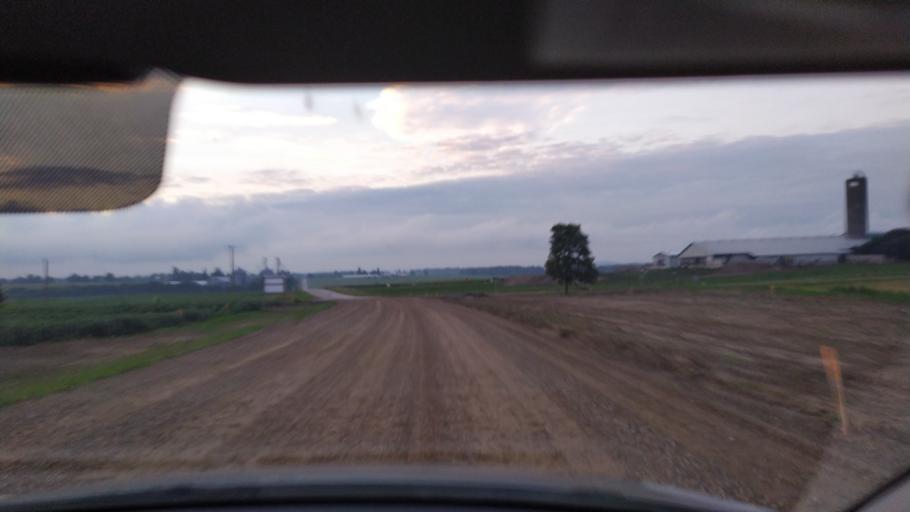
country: CA
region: Ontario
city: Kitchener
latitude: 43.3281
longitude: -80.6188
